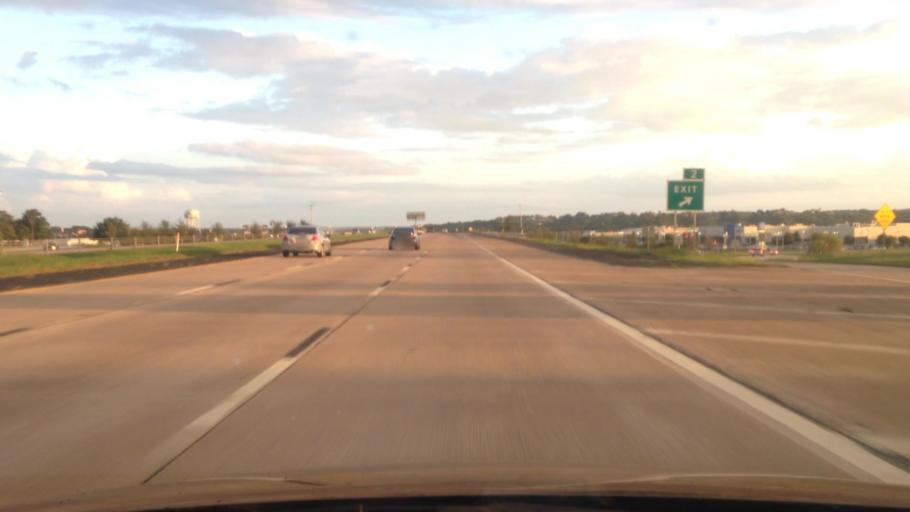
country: US
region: Texas
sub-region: Tarrant County
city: White Settlement
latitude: 32.7279
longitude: -97.4811
